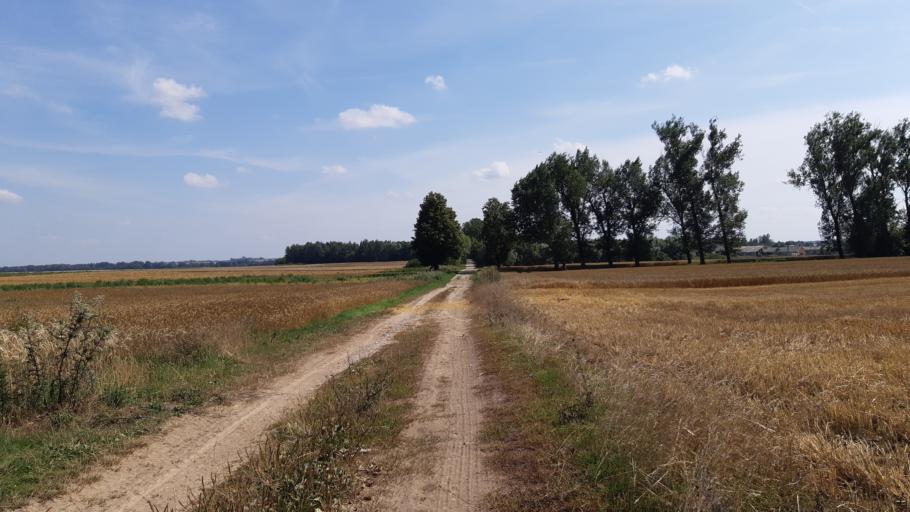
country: LT
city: Virbalis
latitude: 54.6410
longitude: 22.8202
